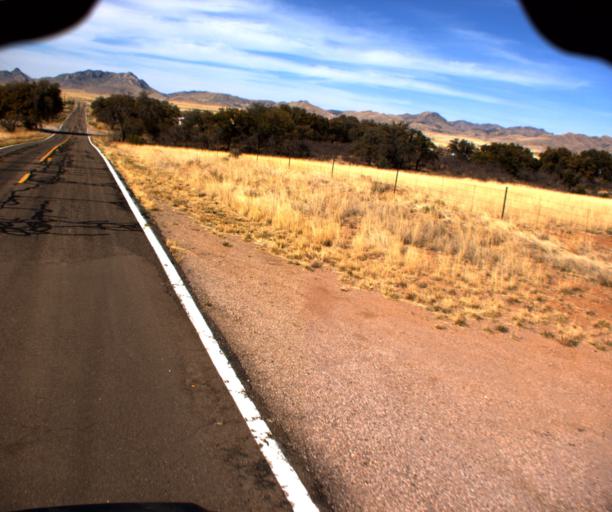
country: US
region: Arizona
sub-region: Cochise County
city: Willcox
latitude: 31.9996
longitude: -109.4400
